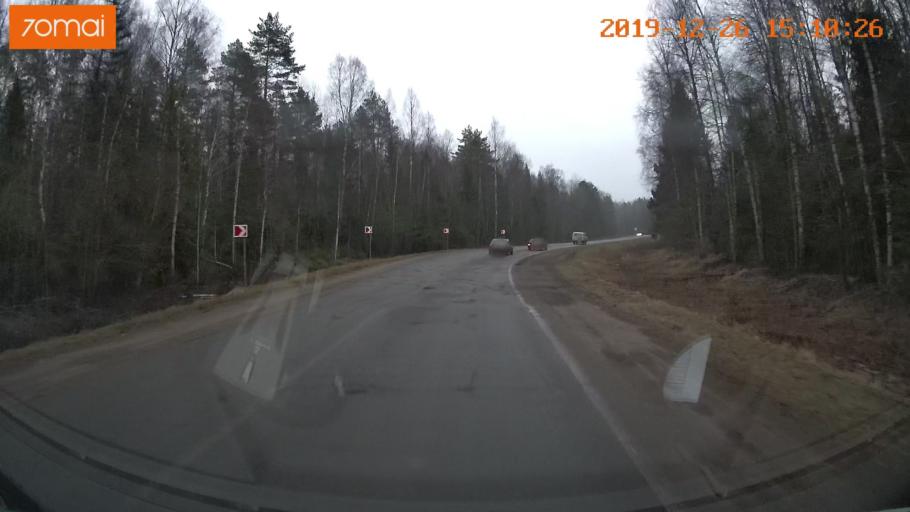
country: RU
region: Jaroslavl
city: Rybinsk
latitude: 58.1404
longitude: 38.8517
